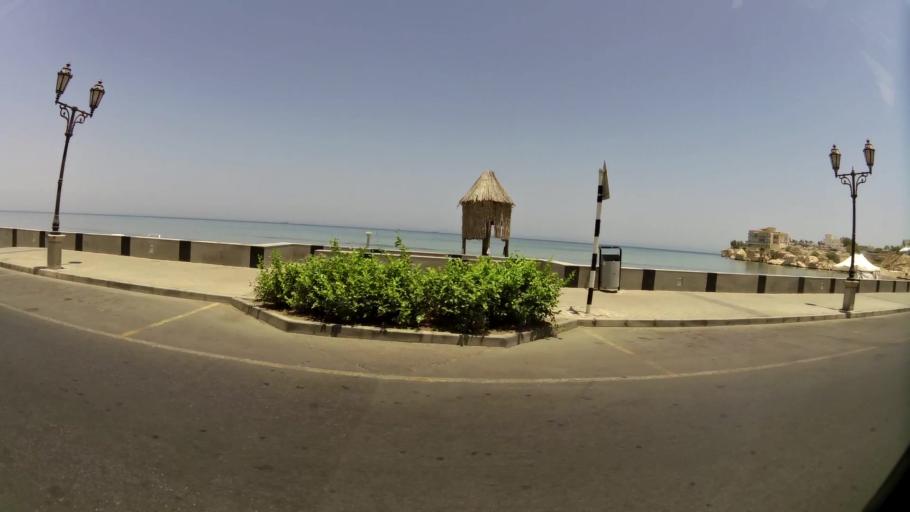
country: OM
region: Muhafazat Masqat
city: Bawshar
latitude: 23.6258
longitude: 58.4806
